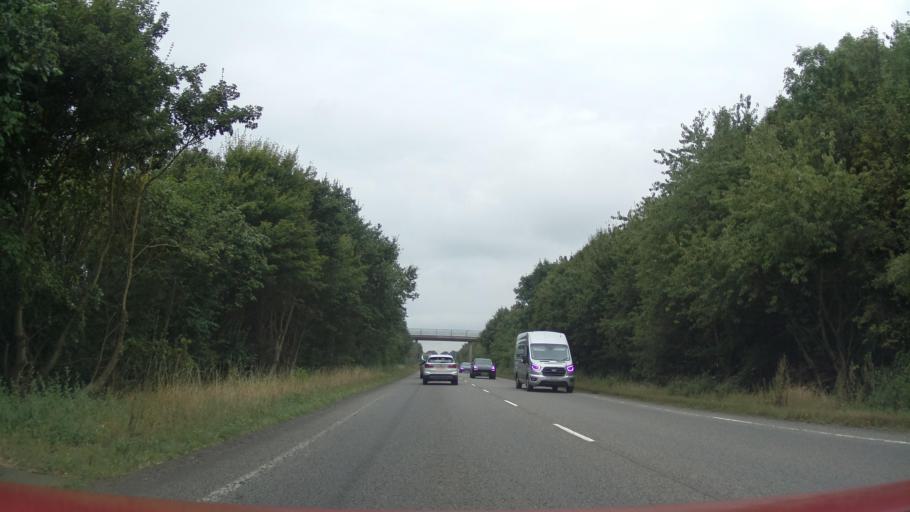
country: GB
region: England
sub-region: Nottinghamshire
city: South Collingham
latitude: 53.0919
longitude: -0.7676
